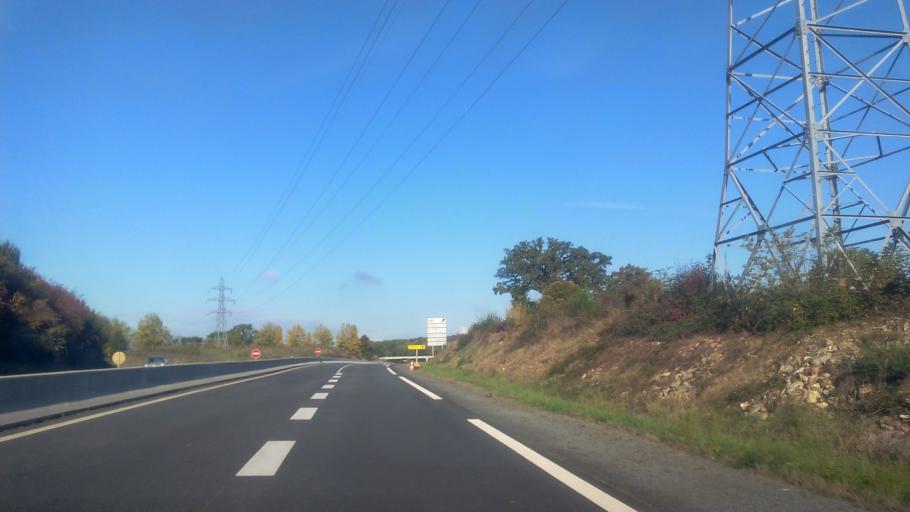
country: FR
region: Pays de la Loire
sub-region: Departement de la Loire-Atlantique
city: Saint-Nicolas-de-Redon
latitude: 47.6737
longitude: -2.0601
